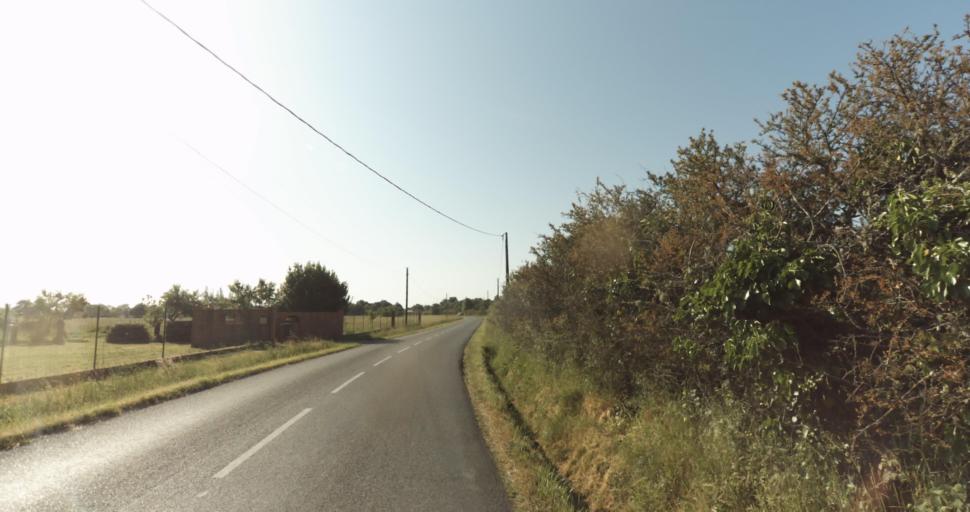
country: FR
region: Midi-Pyrenees
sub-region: Departement de la Haute-Garonne
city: Leguevin
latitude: 43.5772
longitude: 1.2284
